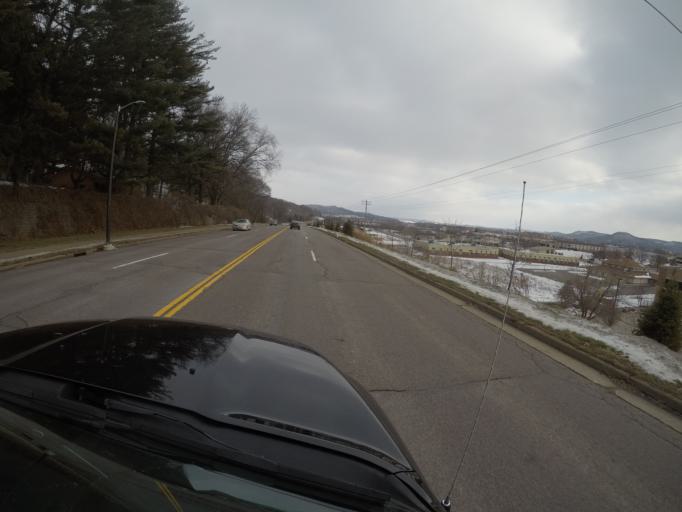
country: US
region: Wisconsin
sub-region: La Crosse County
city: Onalaska
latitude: 43.8809
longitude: -91.1932
